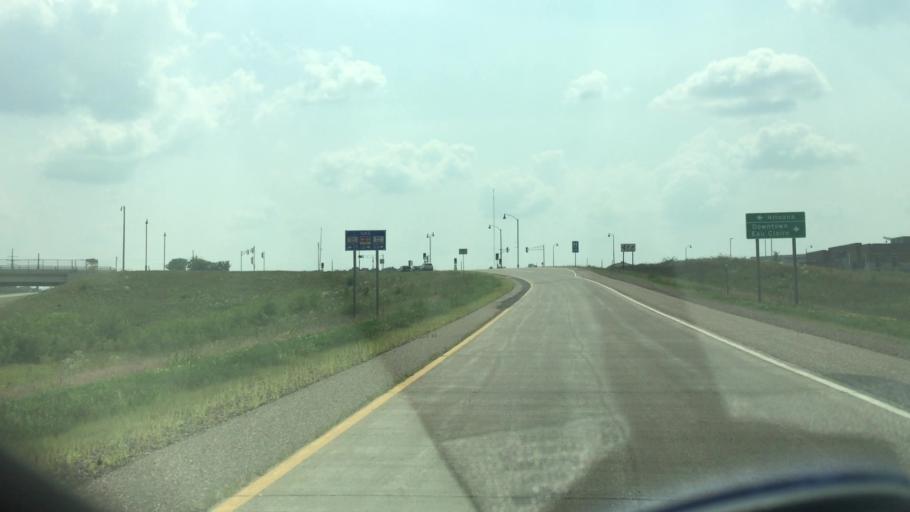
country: US
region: Wisconsin
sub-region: Eau Claire County
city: Altoona
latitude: 44.8198
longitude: -91.4551
